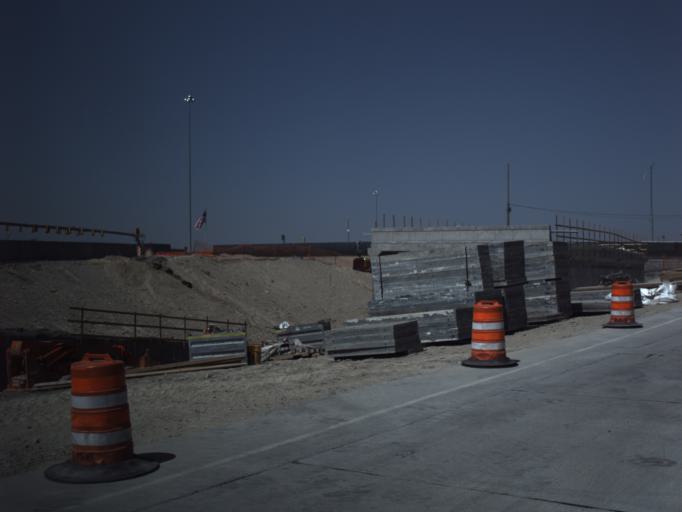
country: US
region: Utah
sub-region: Salt Lake County
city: South Jordan
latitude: 40.5579
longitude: -111.8969
